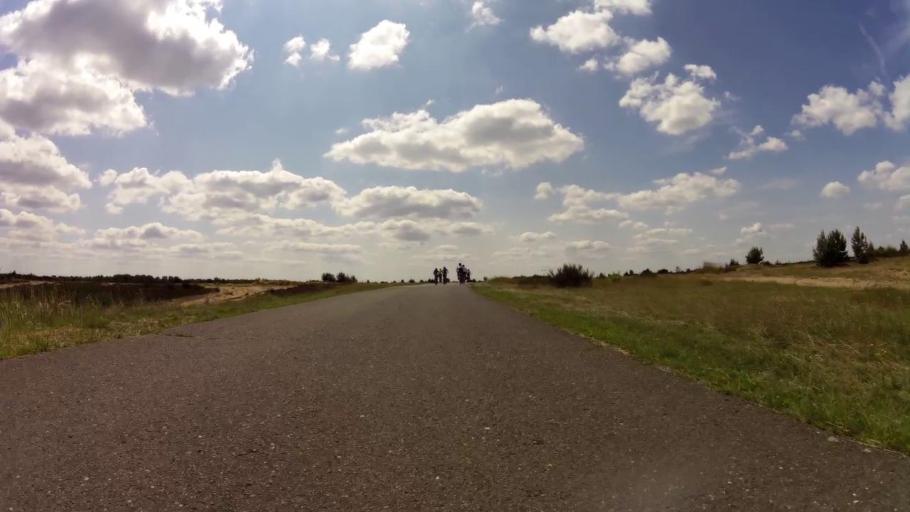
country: PL
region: West Pomeranian Voivodeship
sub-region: Powiat drawski
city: Drawsko Pomorskie
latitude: 53.4220
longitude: 15.7444
